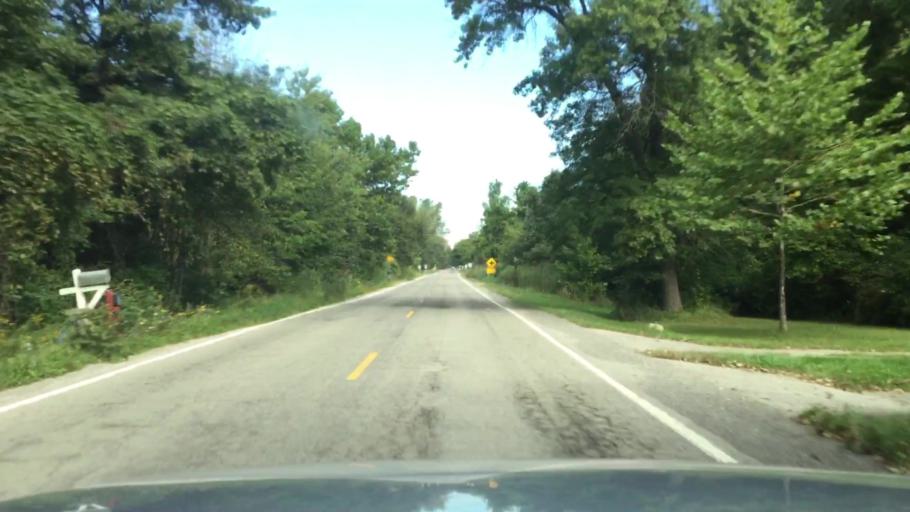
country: US
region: Michigan
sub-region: Wayne County
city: Belleville
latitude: 42.1578
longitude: -83.4613
